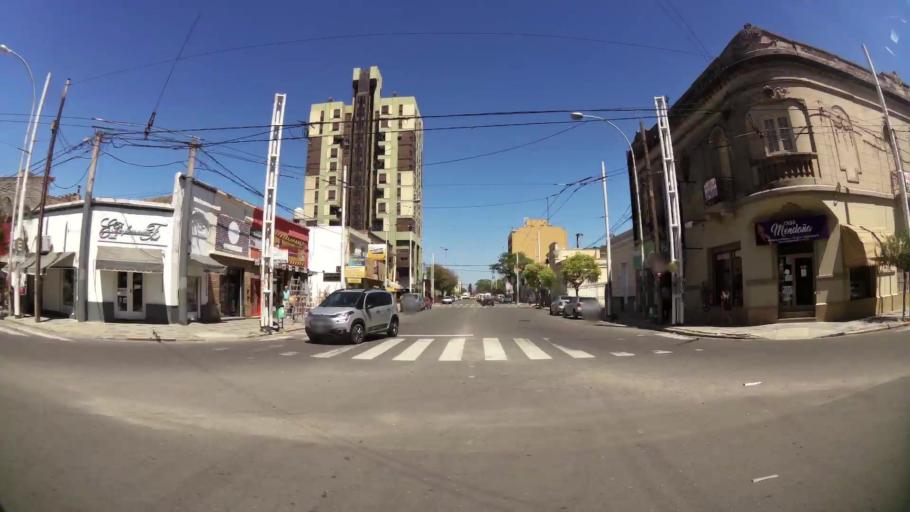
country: AR
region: Cordoba
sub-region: Departamento de Capital
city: Cordoba
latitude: -31.4234
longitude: -64.1486
